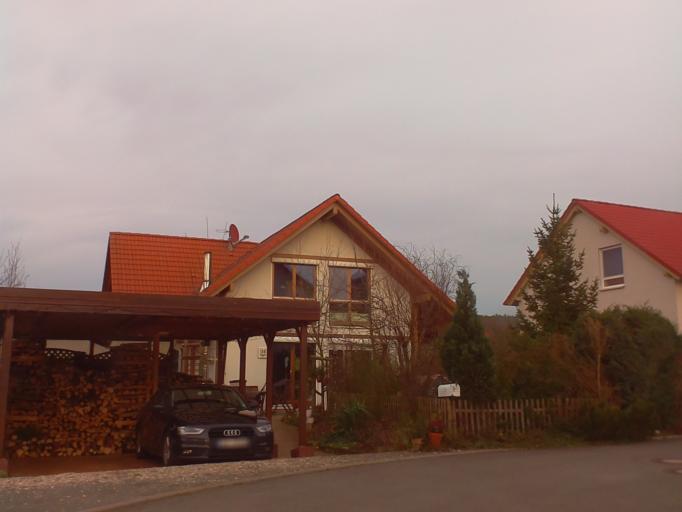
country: DE
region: Thuringia
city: Grosspurschutz
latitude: 50.8241
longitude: 11.6017
